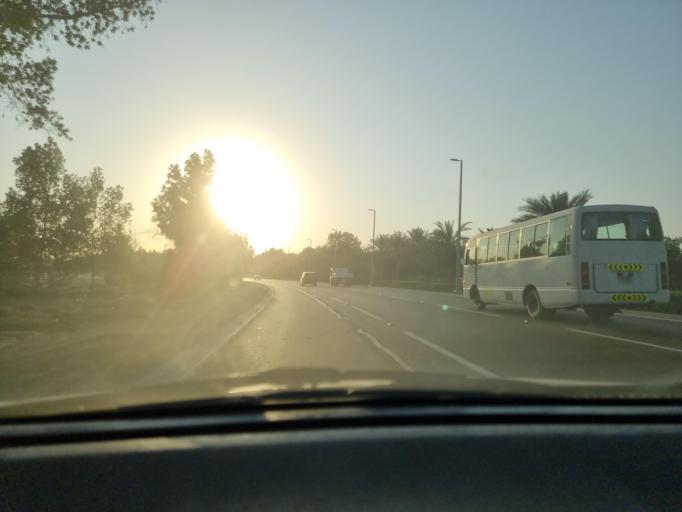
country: AE
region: Abu Dhabi
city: Abu Dhabi
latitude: 24.4134
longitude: 54.6251
